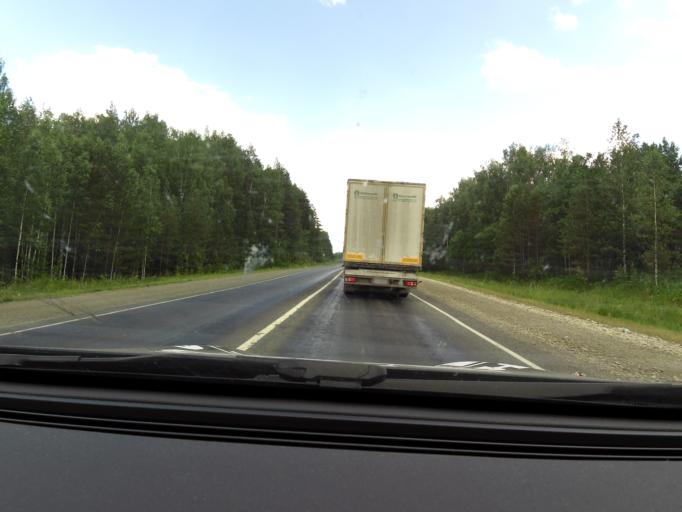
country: RU
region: Sverdlovsk
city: Bisert'
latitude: 56.8369
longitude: 58.8778
